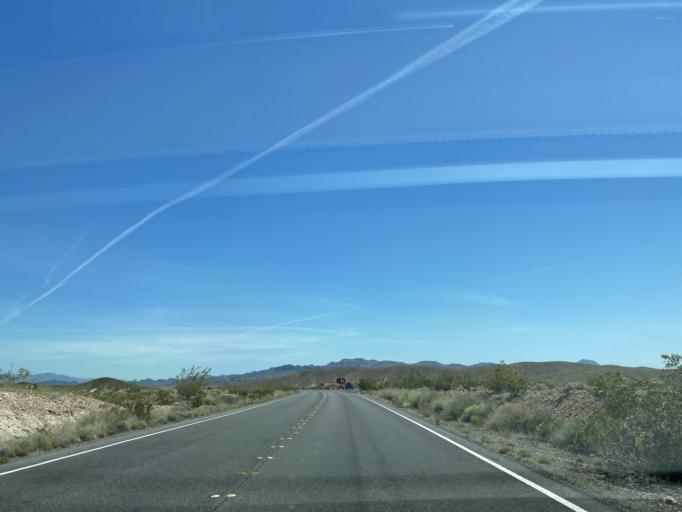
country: US
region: Nevada
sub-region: Clark County
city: Henderson
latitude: 36.1690
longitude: -114.9115
